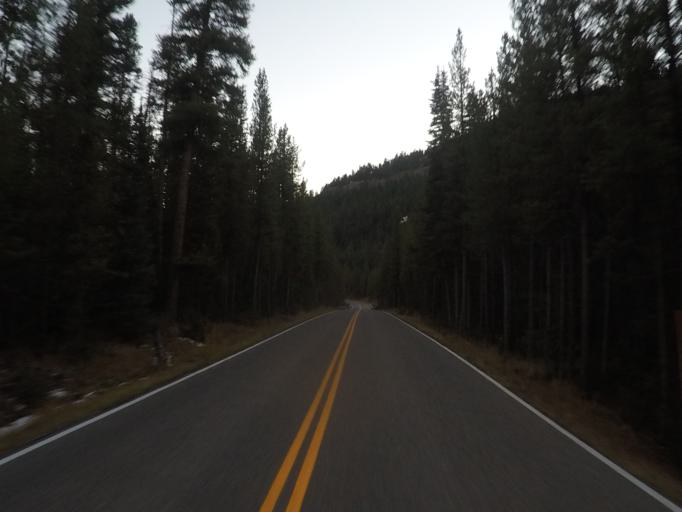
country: US
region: Montana
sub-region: Stillwater County
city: Absarokee
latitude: 44.9467
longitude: -110.0808
